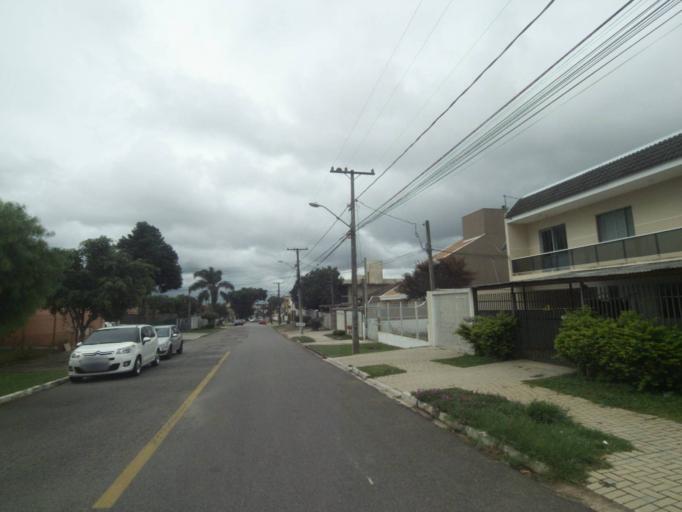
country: BR
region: Parana
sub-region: Curitiba
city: Curitiba
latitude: -25.4955
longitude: -49.3065
